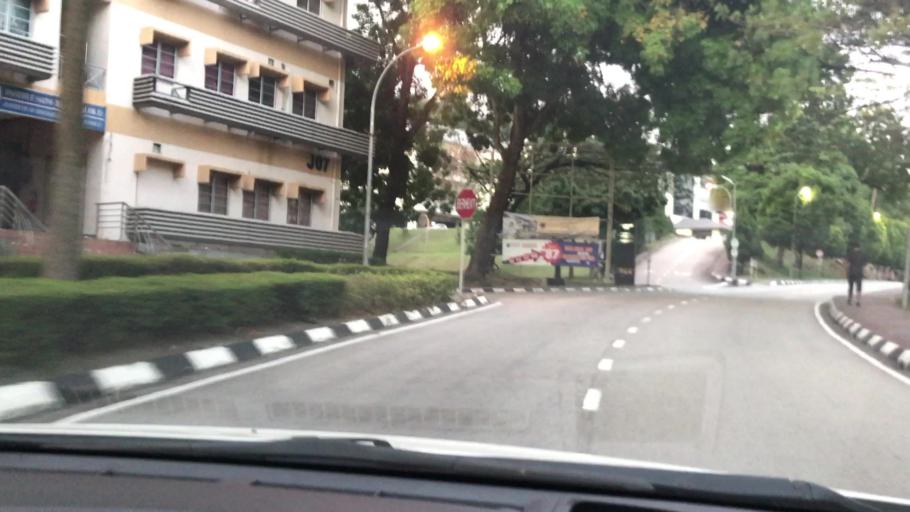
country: MY
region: Kuala Lumpur
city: Kuala Lumpur
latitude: 3.1218
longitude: 101.6552
